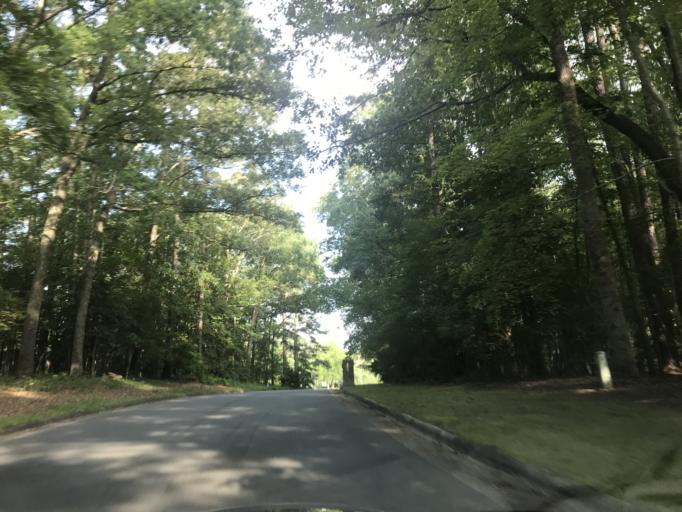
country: US
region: North Carolina
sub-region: Wake County
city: Knightdale
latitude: 35.8322
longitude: -78.5446
